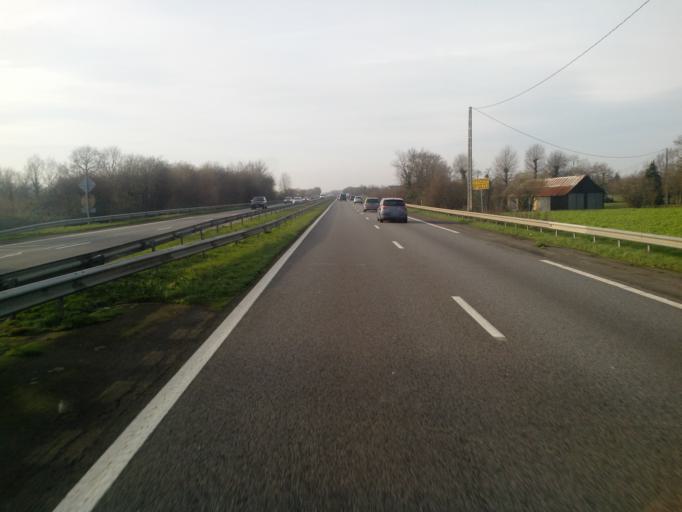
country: FR
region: Brittany
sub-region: Departement d'Ille-et-Vilaine
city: Saint-Gilles
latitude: 48.1587
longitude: -1.8242
